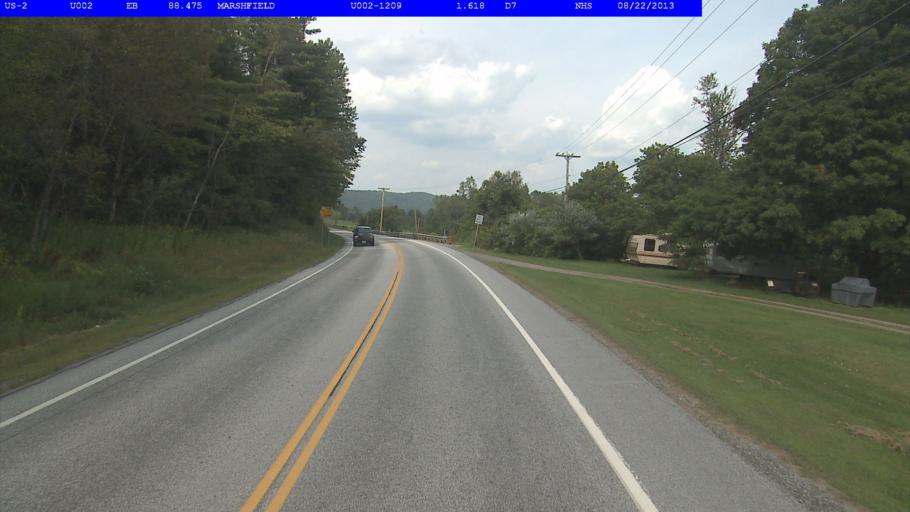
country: US
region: Vermont
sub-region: Washington County
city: Barre
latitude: 44.2942
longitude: -72.3982
